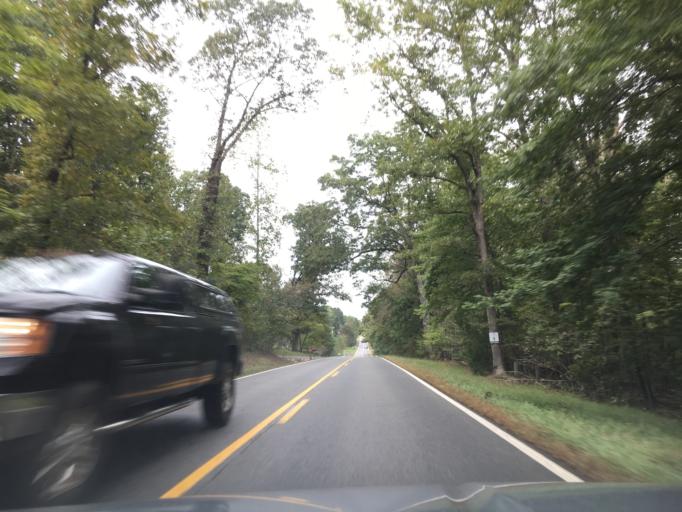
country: US
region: Virginia
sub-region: Goochland County
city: Goochland
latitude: 37.7627
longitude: -77.8777
